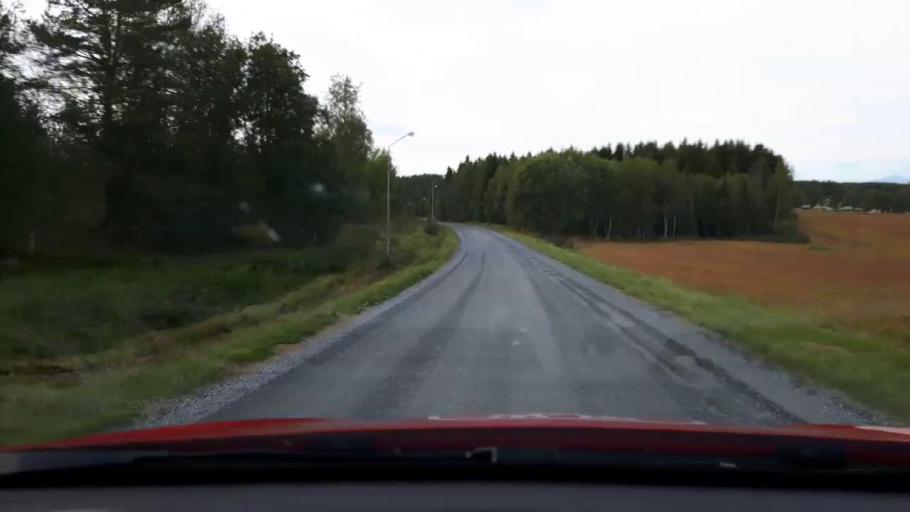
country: SE
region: Jaemtland
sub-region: Krokoms Kommun
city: Valla
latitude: 63.2439
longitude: 13.9878
